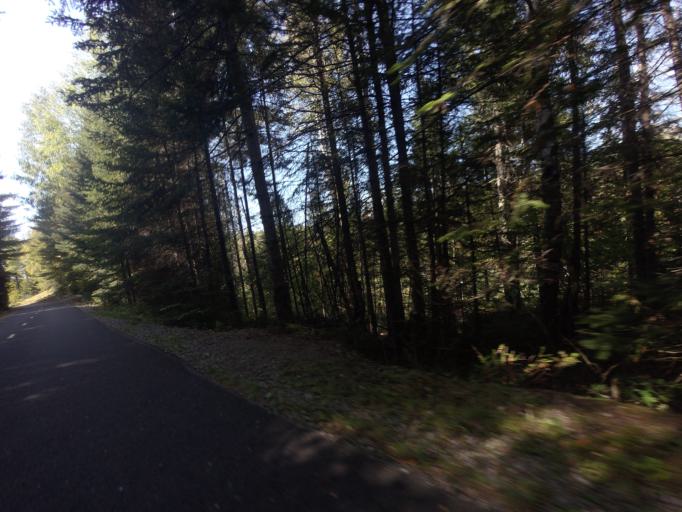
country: CA
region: Quebec
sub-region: Laurentides
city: Mont-Tremblant
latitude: 46.1260
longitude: -74.5346
